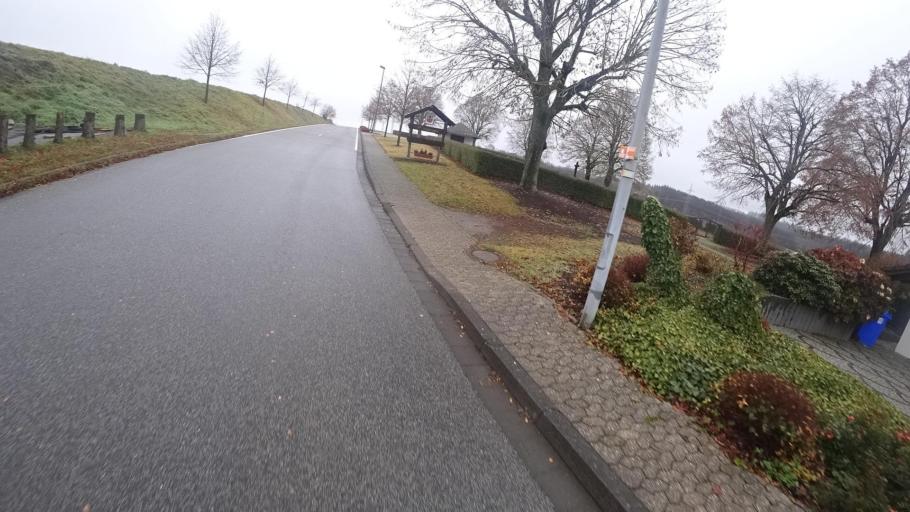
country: DE
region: Rheinland-Pfalz
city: Norath
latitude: 50.1268
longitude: 7.5806
